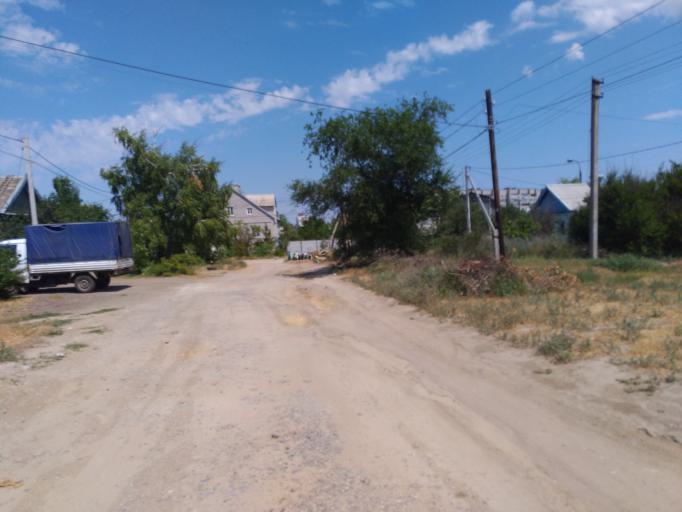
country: RU
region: Volgograd
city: Volgograd
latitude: 48.6488
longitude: 44.4283
